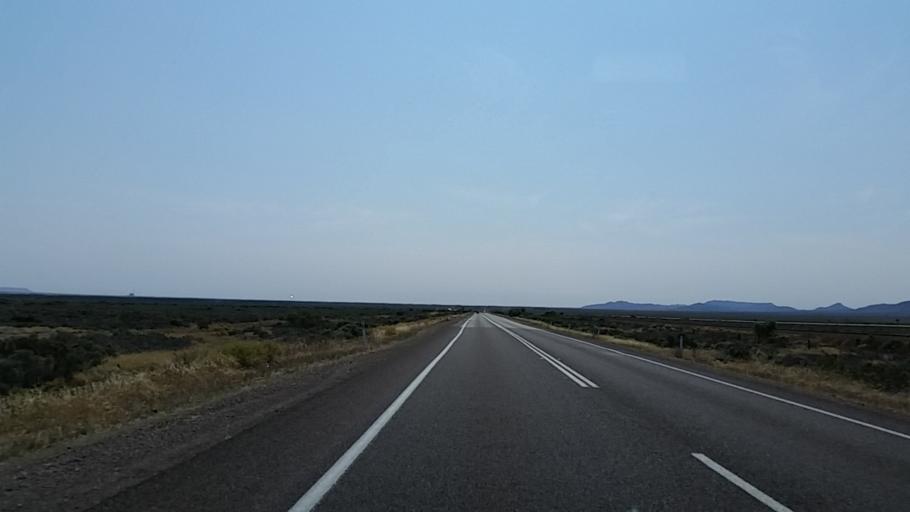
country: AU
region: South Australia
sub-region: Port Augusta
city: Port Augusta
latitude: -32.6888
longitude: 137.9404
